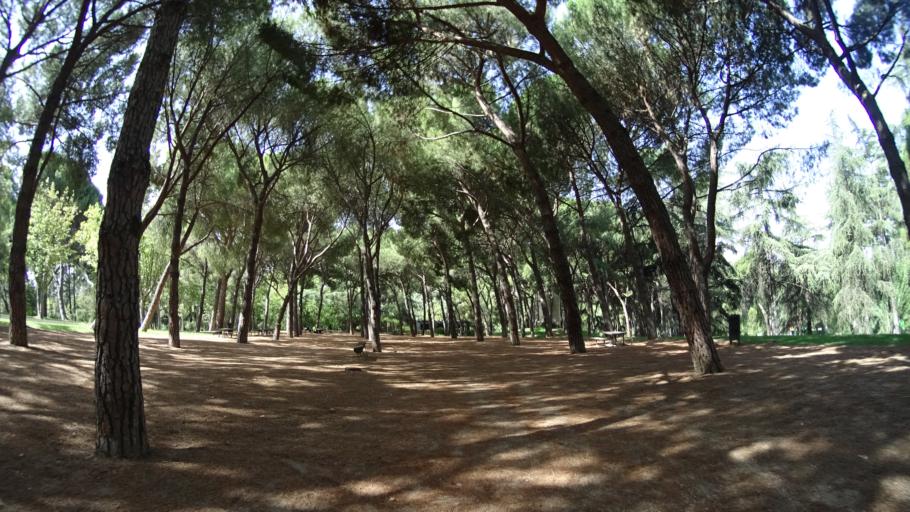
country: ES
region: Madrid
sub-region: Provincia de Madrid
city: Moncloa-Aravaca
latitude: 40.4349
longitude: -3.7287
